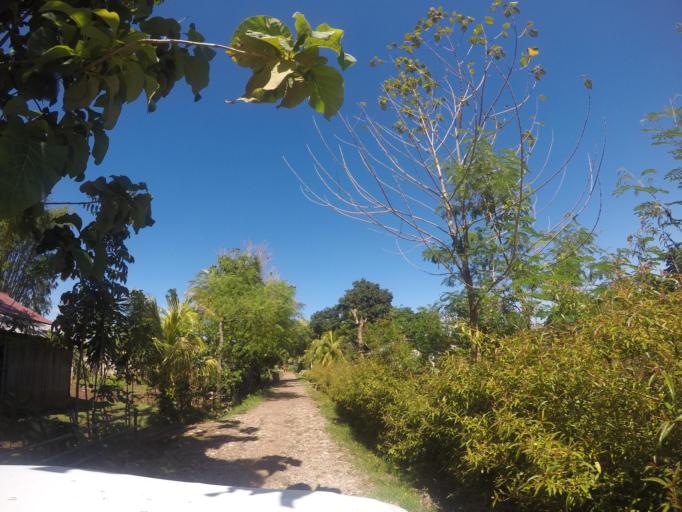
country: TL
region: Bobonaro
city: Maliana
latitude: -8.9888
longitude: 125.2027
